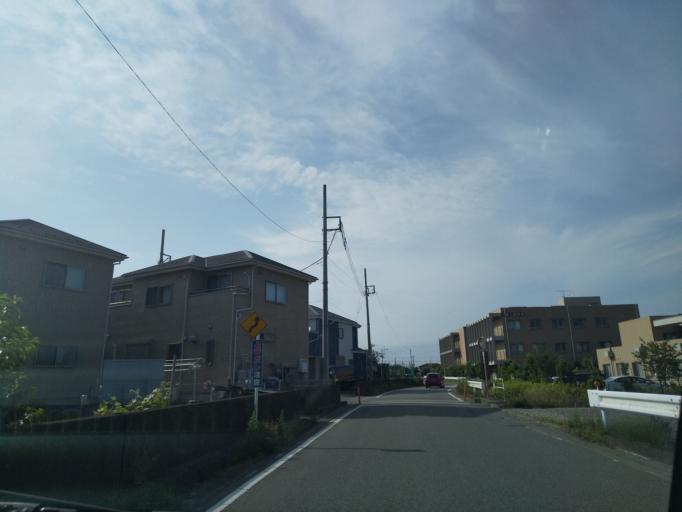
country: JP
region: Kanagawa
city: Zama
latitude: 35.4786
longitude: 139.3804
